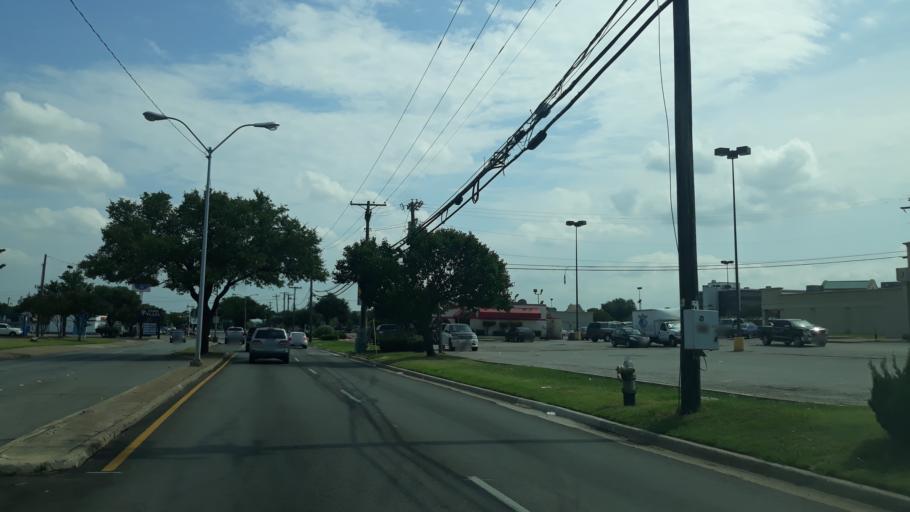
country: US
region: Texas
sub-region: Dallas County
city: Irving
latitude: 32.8311
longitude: -96.9765
